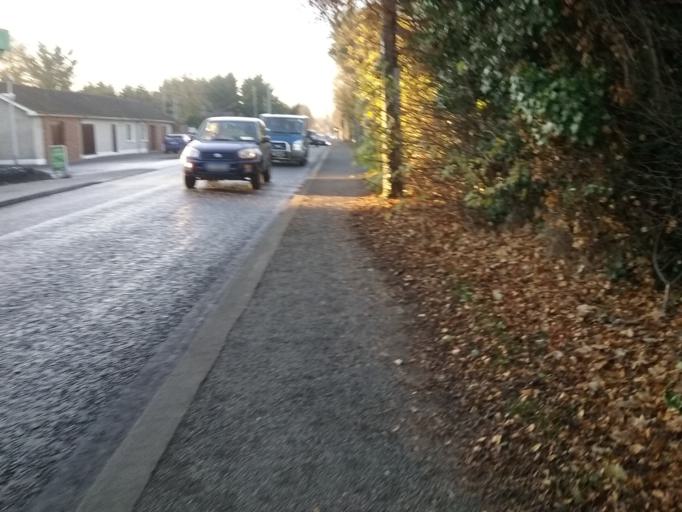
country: IE
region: Leinster
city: Hartstown
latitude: 53.3835
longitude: -6.4175
